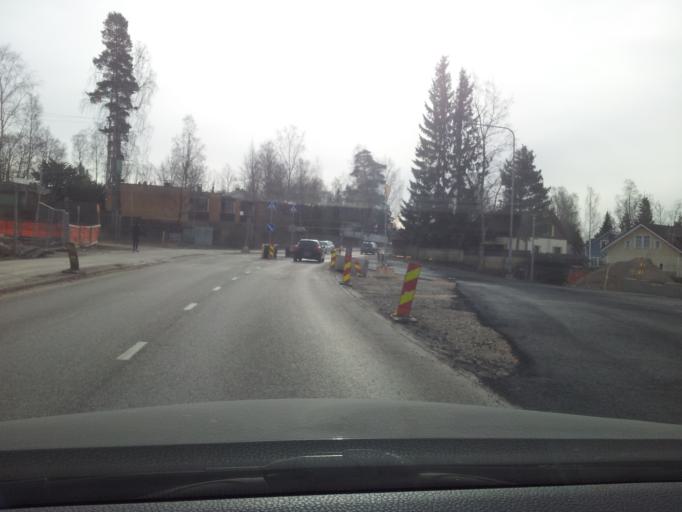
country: FI
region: Uusimaa
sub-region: Helsinki
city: Kilo
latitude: 60.1890
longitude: 24.7811
